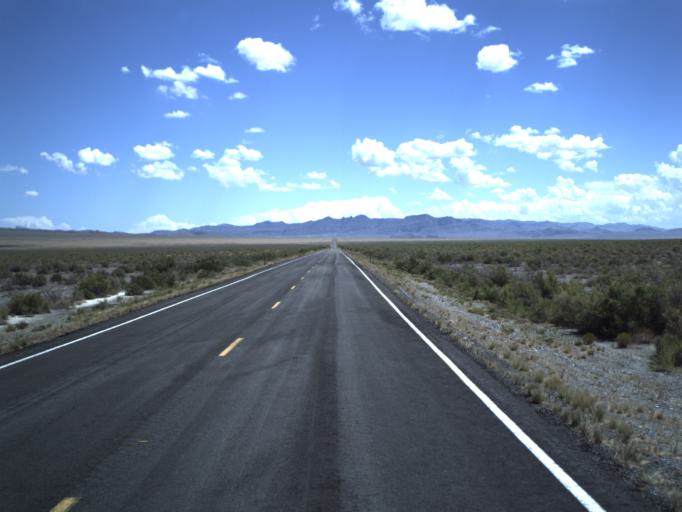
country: US
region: Nevada
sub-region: White Pine County
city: McGill
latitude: 39.0471
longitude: -113.9176
